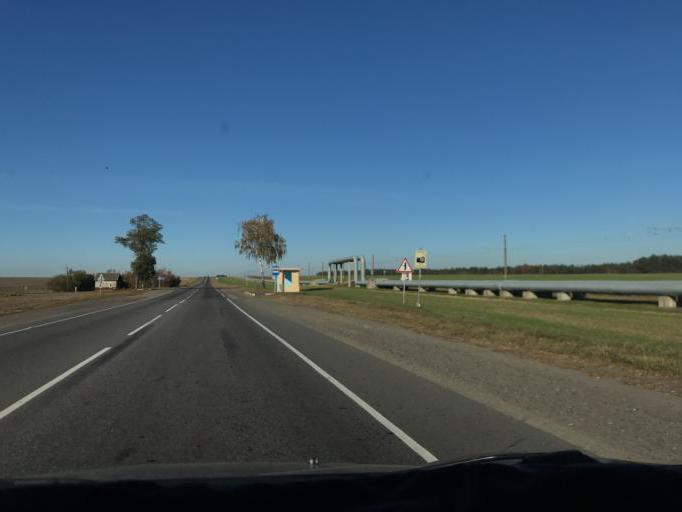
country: BY
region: Gomel
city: Mazyr
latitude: 51.9558
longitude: 29.2621
